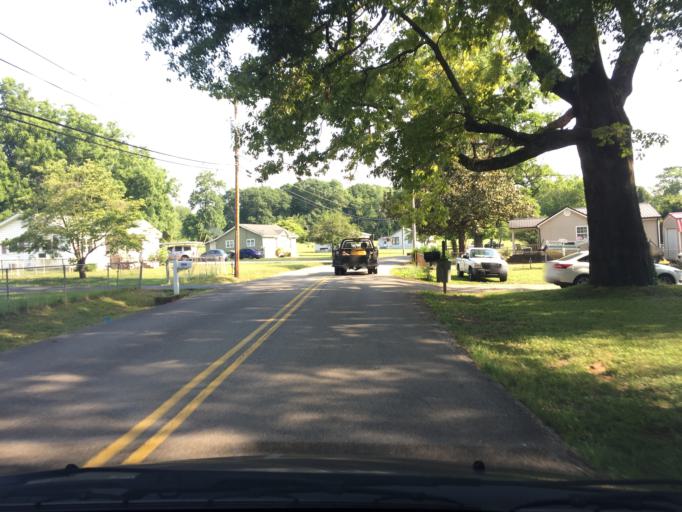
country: US
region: Tennessee
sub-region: Hamilton County
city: Red Bank
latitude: 35.1263
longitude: -85.2329
